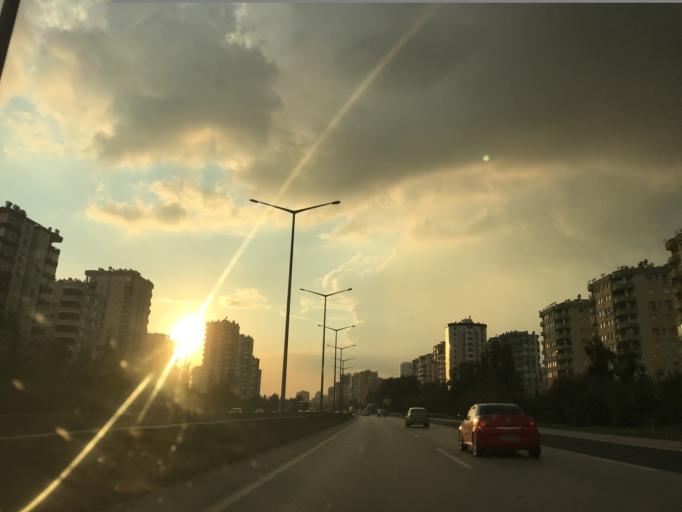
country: TR
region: Adana
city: Adana
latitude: 37.0329
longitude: 35.2986
